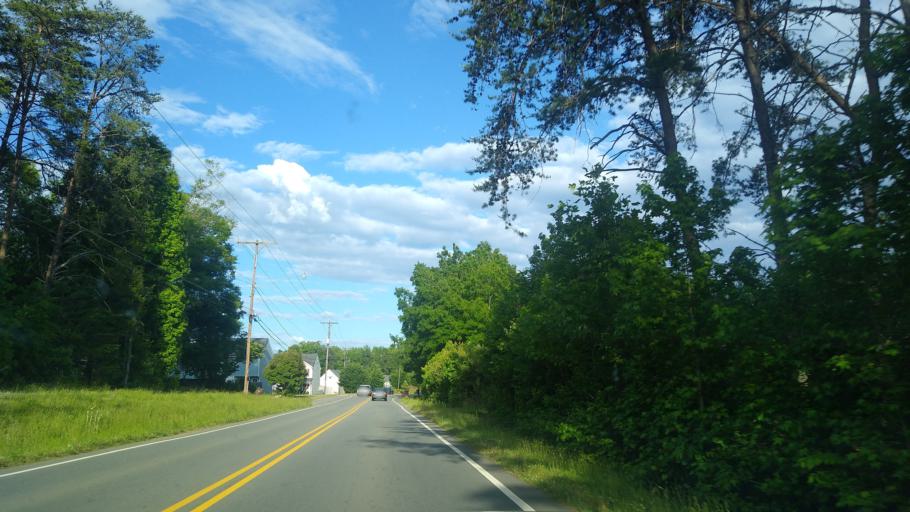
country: US
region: North Carolina
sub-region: Guilford County
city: Greensboro
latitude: 36.1466
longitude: -79.7485
